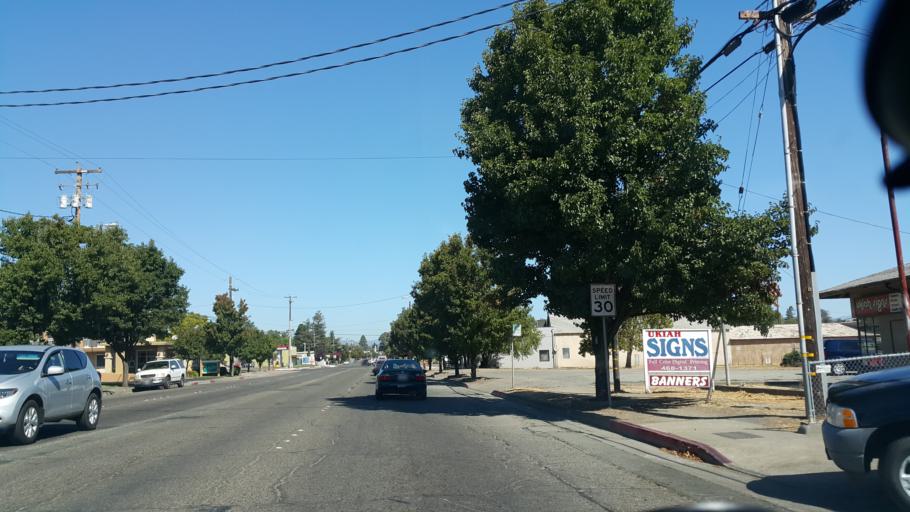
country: US
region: California
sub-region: Mendocino County
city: Ukiah
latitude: 39.1366
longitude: -123.2054
